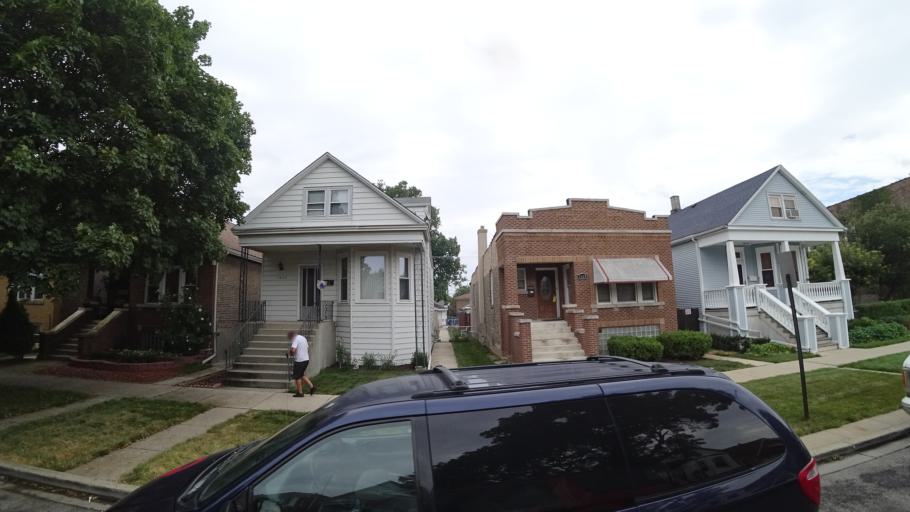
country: US
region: Illinois
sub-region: Cook County
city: Cicero
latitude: 41.8561
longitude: -87.7653
